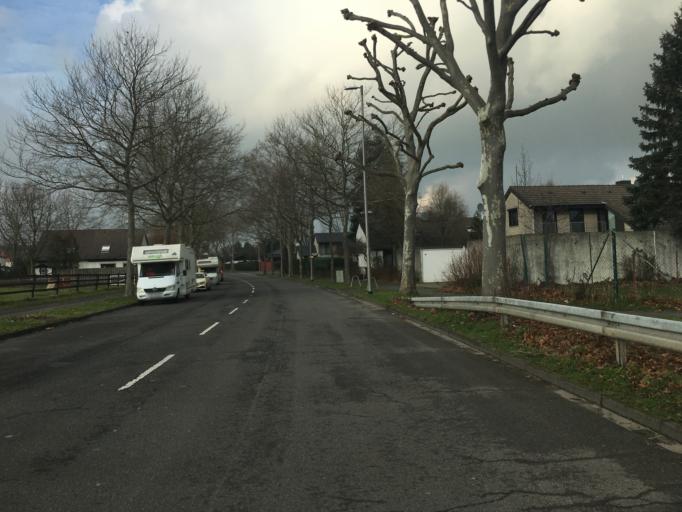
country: DE
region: North Rhine-Westphalia
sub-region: Regierungsbezirk Koln
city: Mengenich
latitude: 51.0318
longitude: 6.8932
